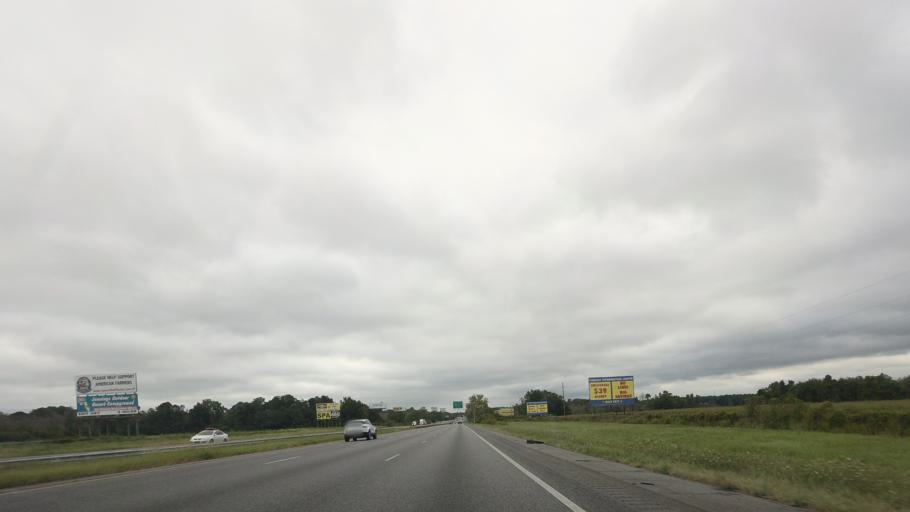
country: US
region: Georgia
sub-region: Echols County
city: Statenville
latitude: 30.6576
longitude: -83.2029
